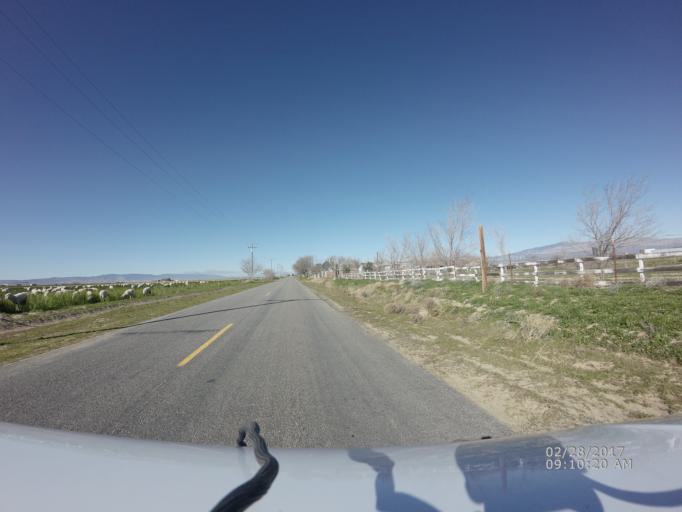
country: US
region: California
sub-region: Kern County
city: Rosamond
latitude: 34.8201
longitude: -118.2925
